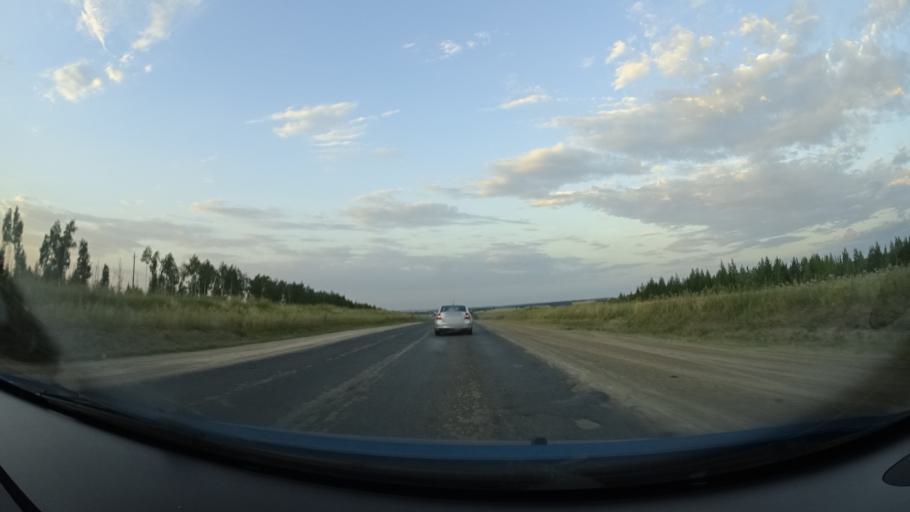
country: RU
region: Orenburg
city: Severnoye
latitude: 54.2259
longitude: 52.7516
